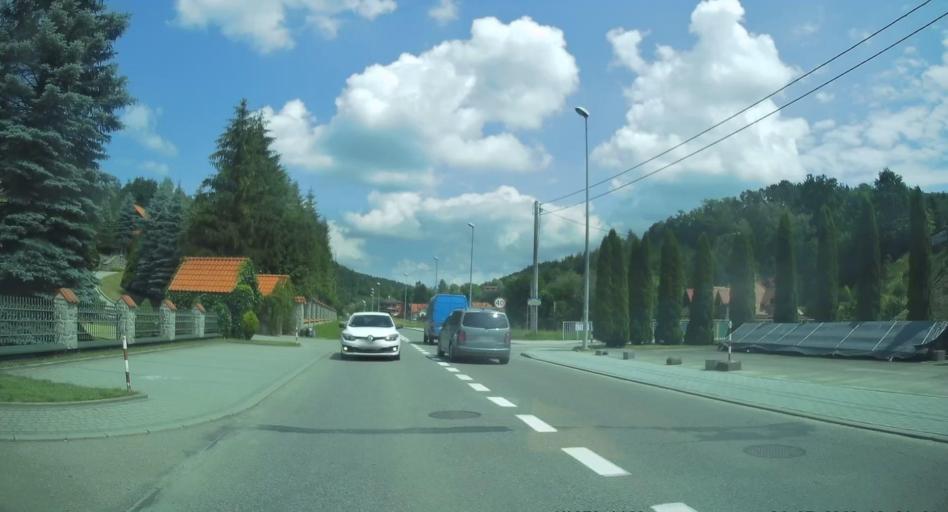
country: PL
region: Lesser Poland Voivodeship
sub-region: Powiat nowosadecki
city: Nowy Sacz
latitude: 49.6376
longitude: 20.7144
